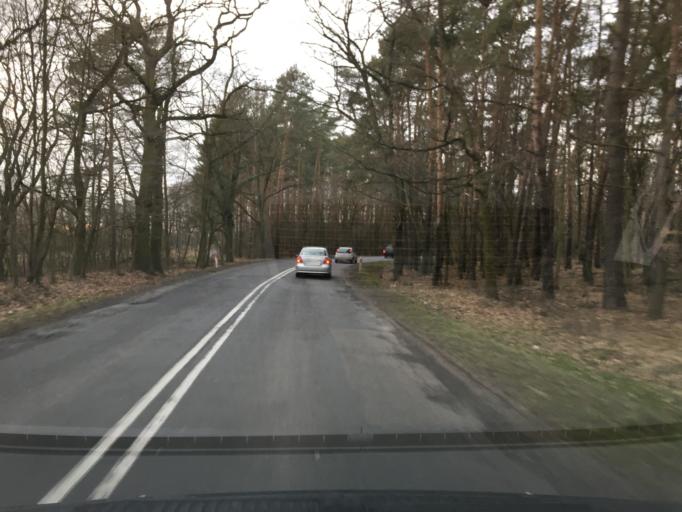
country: PL
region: Opole Voivodeship
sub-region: Powiat krapkowicki
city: Januszkowice
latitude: 50.3682
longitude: 18.1485
